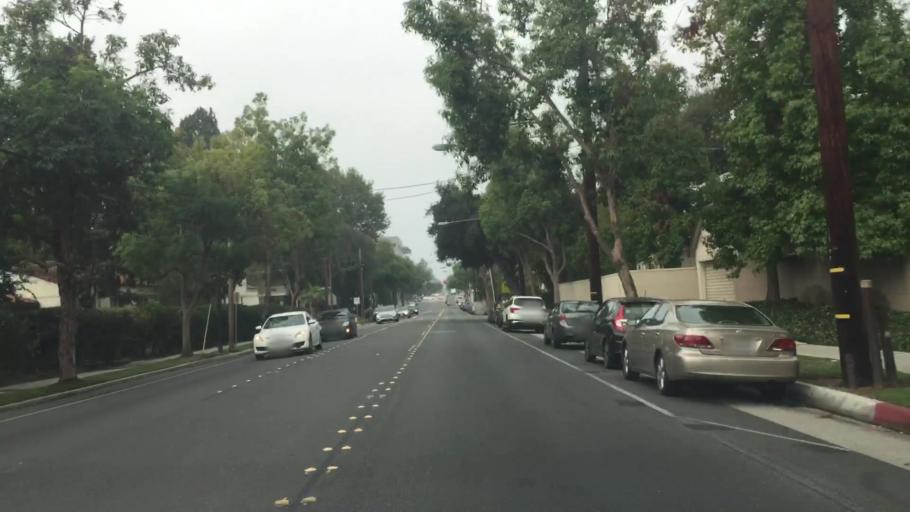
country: US
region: California
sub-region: Los Angeles County
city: Pasadena
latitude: 34.1359
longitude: -118.1283
